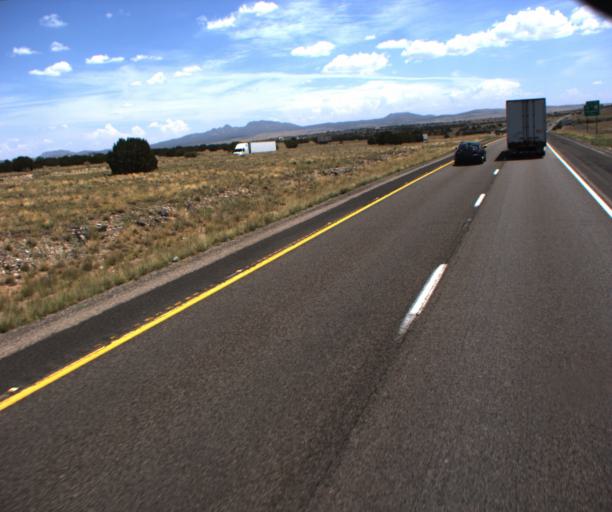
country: US
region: Arizona
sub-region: Mohave County
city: Peach Springs
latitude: 35.3224
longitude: -112.9150
